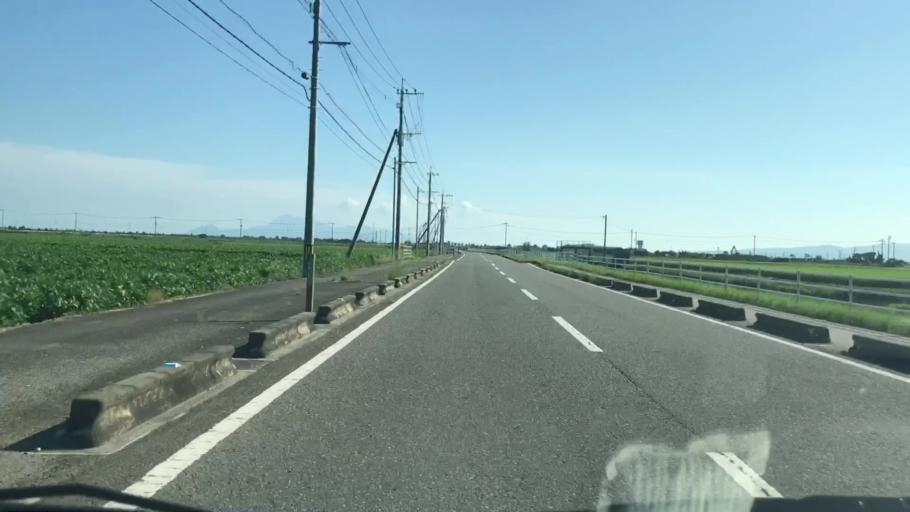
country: JP
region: Saga Prefecture
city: Okawa
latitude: 33.1680
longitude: 130.3096
